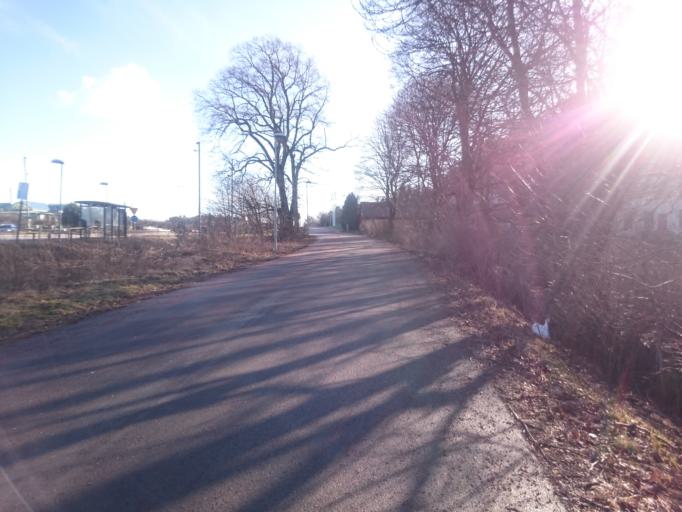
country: SE
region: Vaestra Goetaland
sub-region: Goteborg
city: Goeteborg
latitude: 57.7421
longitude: 11.9398
